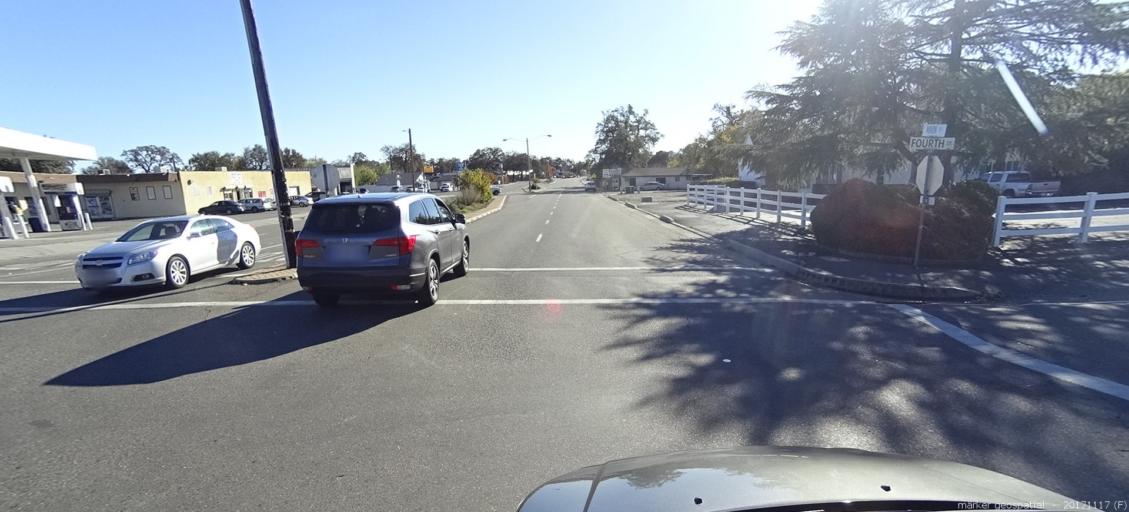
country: US
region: California
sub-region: Shasta County
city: Cottonwood
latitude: 40.3894
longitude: -122.2810
